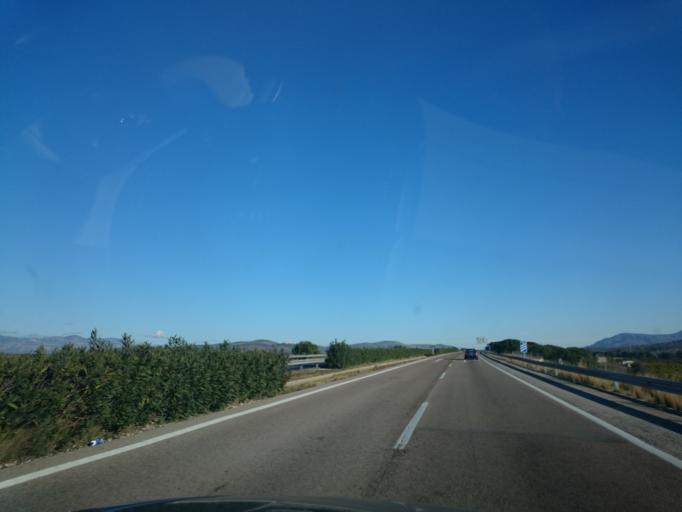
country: ES
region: Catalonia
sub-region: Provincia de Tarragona
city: Ulldecona
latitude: 40.5514
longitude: 0.4225
